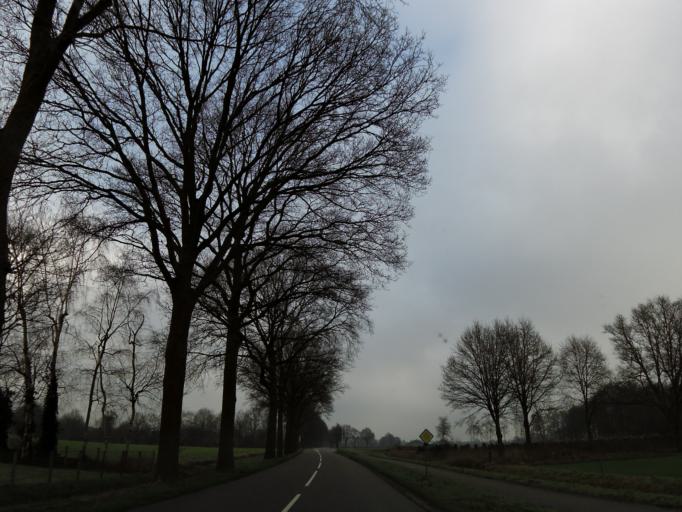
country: NL
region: North Brabant
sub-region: Gemeente Mill en Sint Hubert
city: Wilbertoord
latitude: 51.6498
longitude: 5.7904
